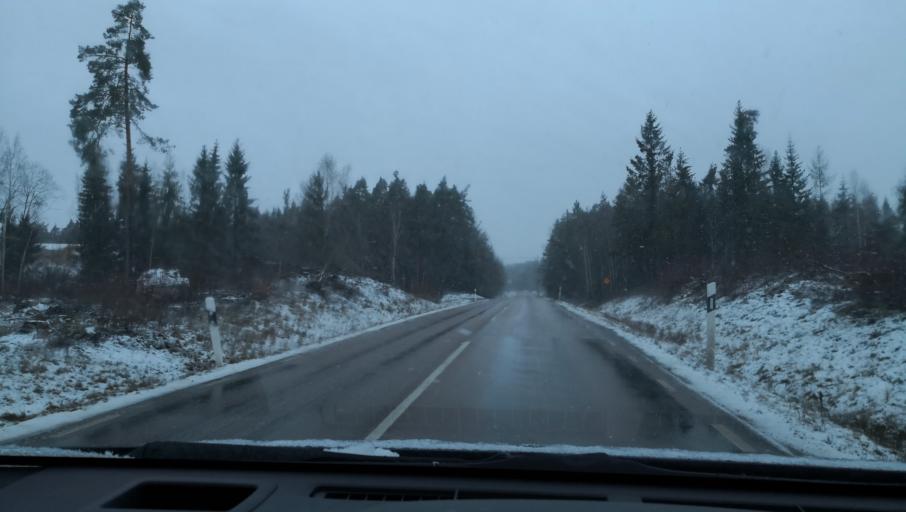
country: SE
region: Vaestmanland
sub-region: Hallstahammars Kommun
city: Kolback
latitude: 59.5831
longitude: 16.3551
